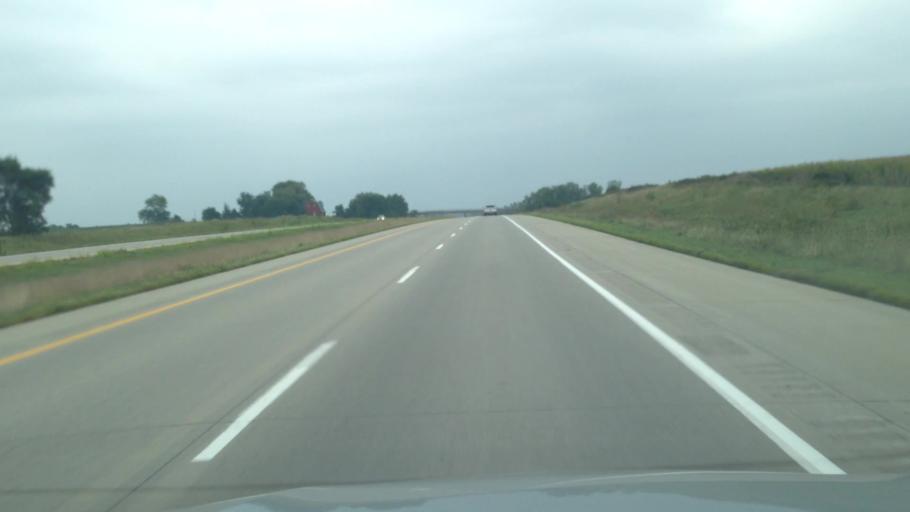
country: US
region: Iowa
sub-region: Clarke County
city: Osceola
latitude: 40.9184
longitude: -93.7974
